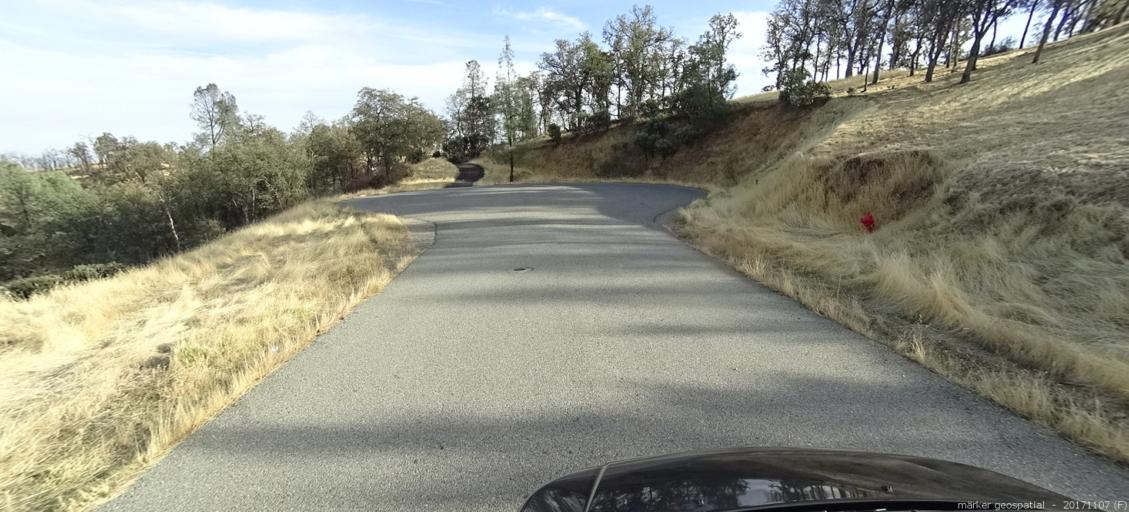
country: US
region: California
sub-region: Shasta County
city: Shasta
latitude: 40.5056
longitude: -122.4715
